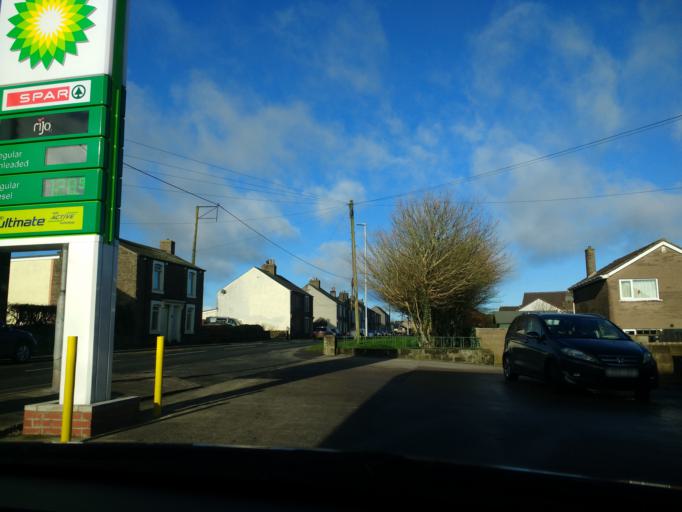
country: GB
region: England
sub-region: Cumbria
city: Dearham
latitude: 54.7054
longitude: -3.4550
